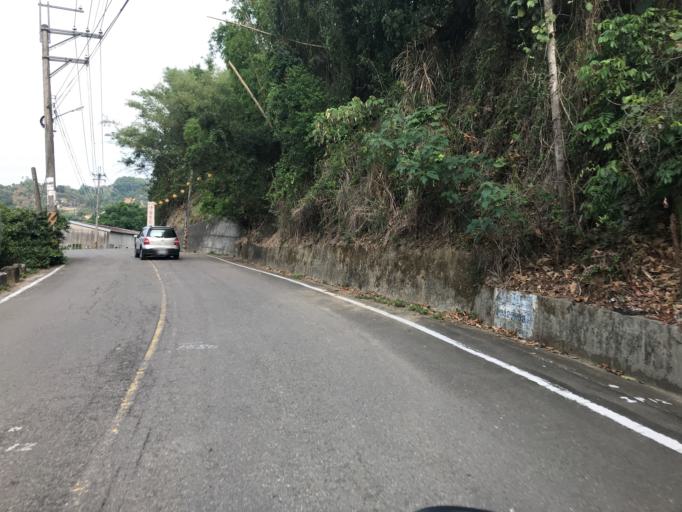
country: TW
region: Taiwan
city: Zhongxing New Village
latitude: 24.0386
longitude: 120.7089
